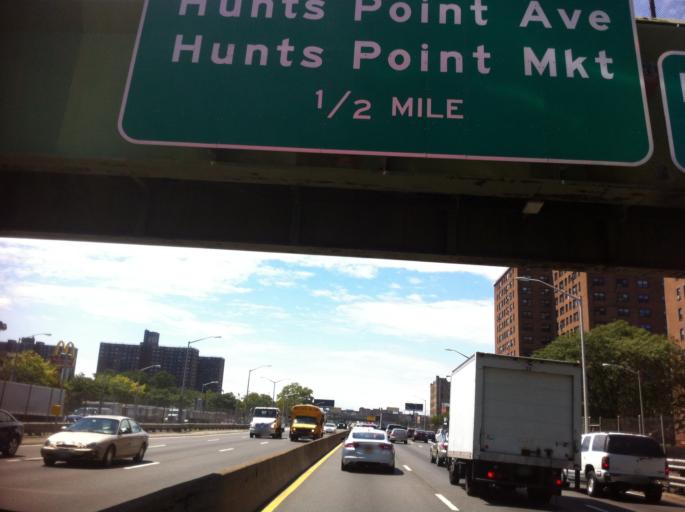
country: US
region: New York
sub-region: Bronx
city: The Bronx
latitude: 40.8241
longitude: -73.8733
